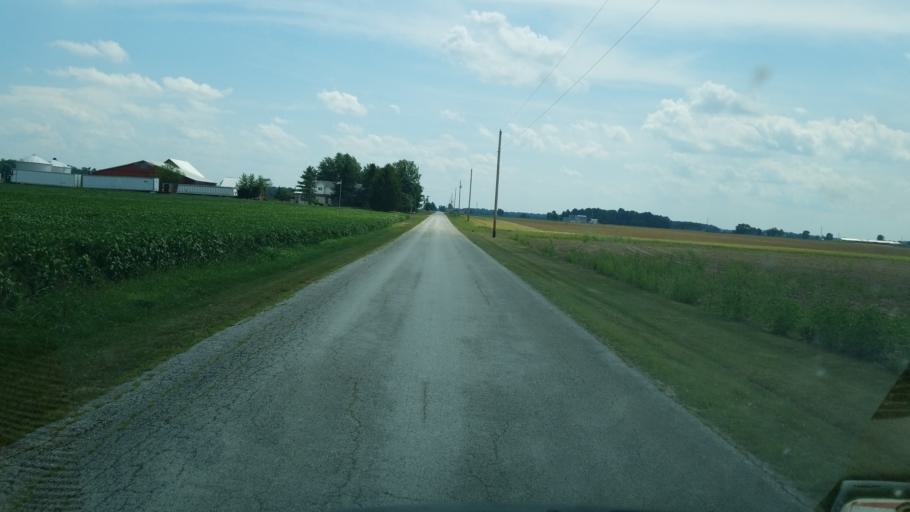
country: US
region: Ohio
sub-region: Wyandot County
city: Carey
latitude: 40.9383
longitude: -83.4672
